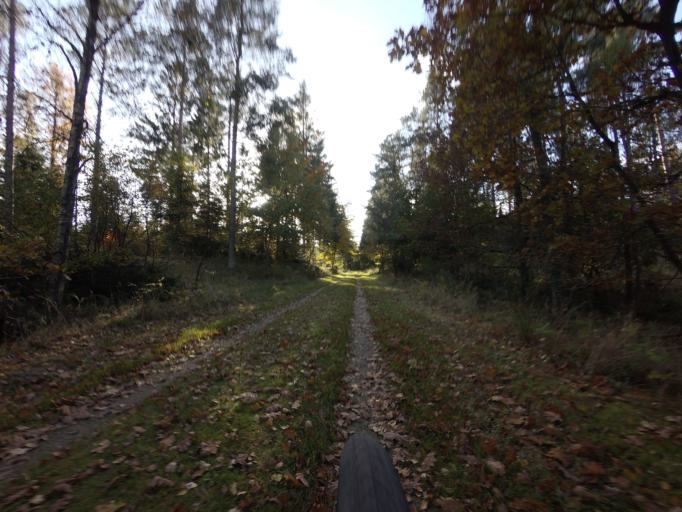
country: DK
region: Central Jutland
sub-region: Norddjurs Kommune
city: Grenaa
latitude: 56.4931
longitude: 10.6934
